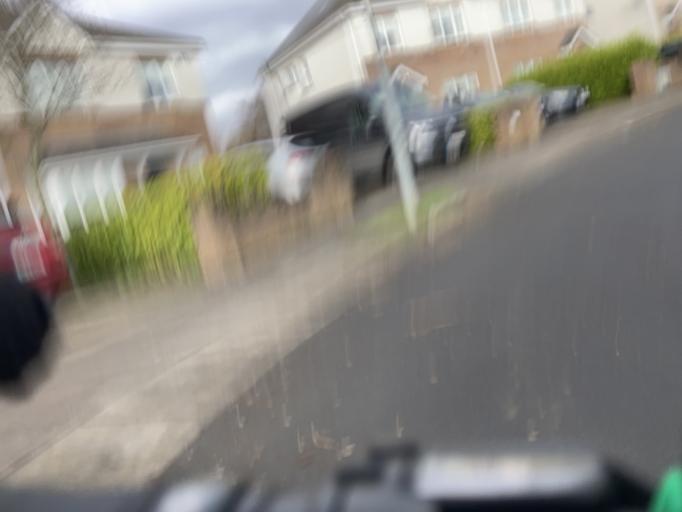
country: IE
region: Leinster
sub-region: Kildare
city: Celbridge
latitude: 53.3457
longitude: -6.5562
